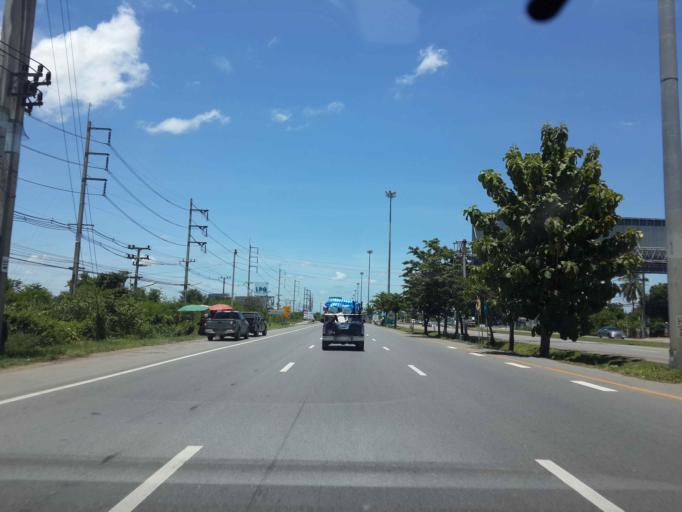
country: TH
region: Ratchaburi
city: Pak Tho
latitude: 13.3281
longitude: 99.8289
